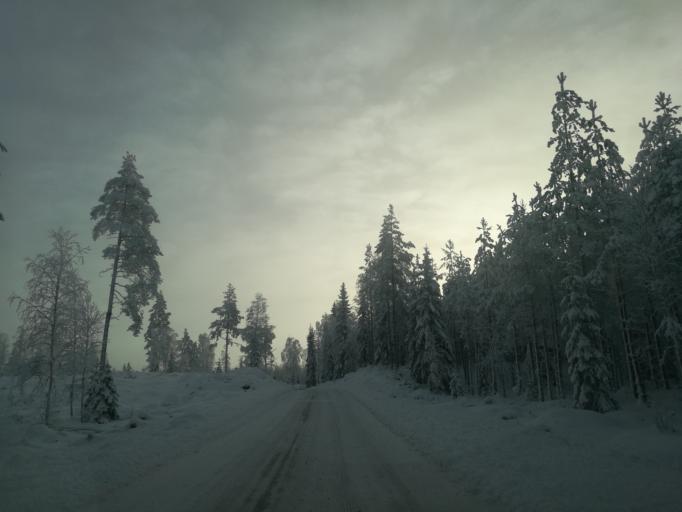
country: SE
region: Vaermland
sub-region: Torsby Kommun
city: Torsby
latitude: 60.6435
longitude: 12.7813
